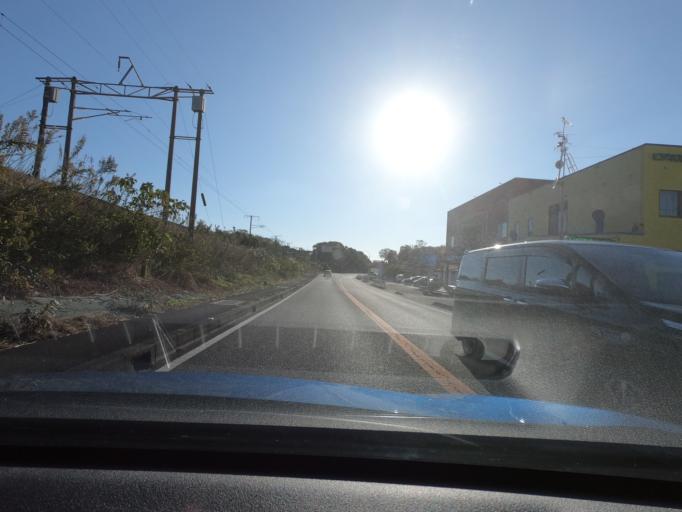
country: JP
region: Kagoshima
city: Izumi
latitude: 32.1332
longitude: 130.3506
